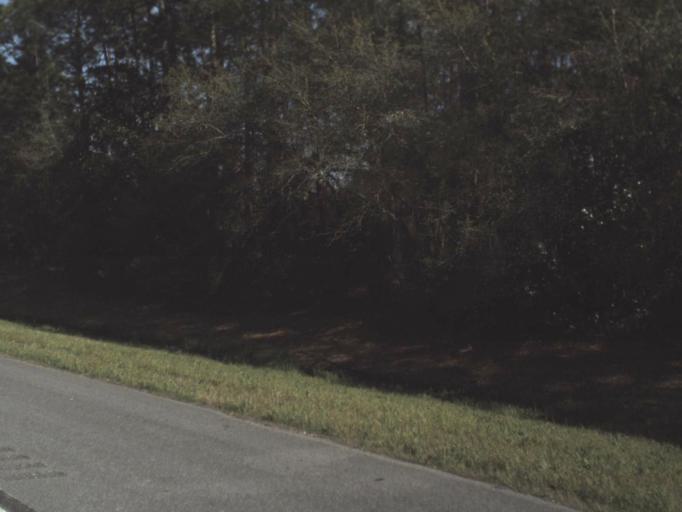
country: US
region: Florida
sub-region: Okaloosa County
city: Crestview
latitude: 30.7264
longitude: -86.5521
